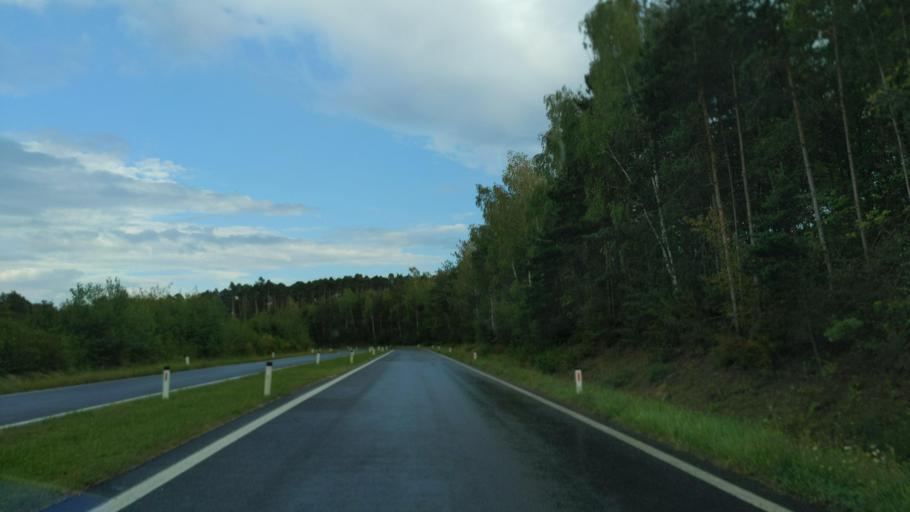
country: AT
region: Burgenland
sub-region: Politischer Bezirk Mattersburg
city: Neudorfl
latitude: 47.7882
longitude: 16.2902
